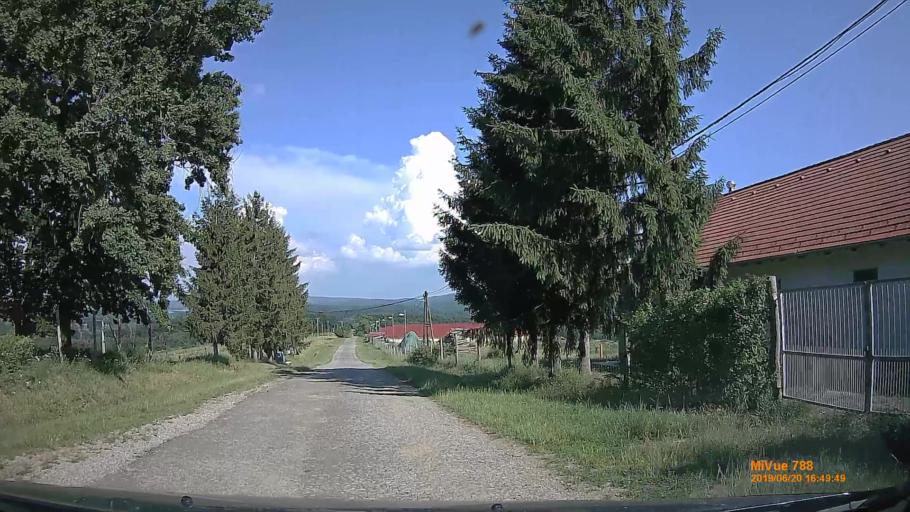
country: HU
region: Baranya
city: Buekkoesd
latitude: 46.1596
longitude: 18.0400
